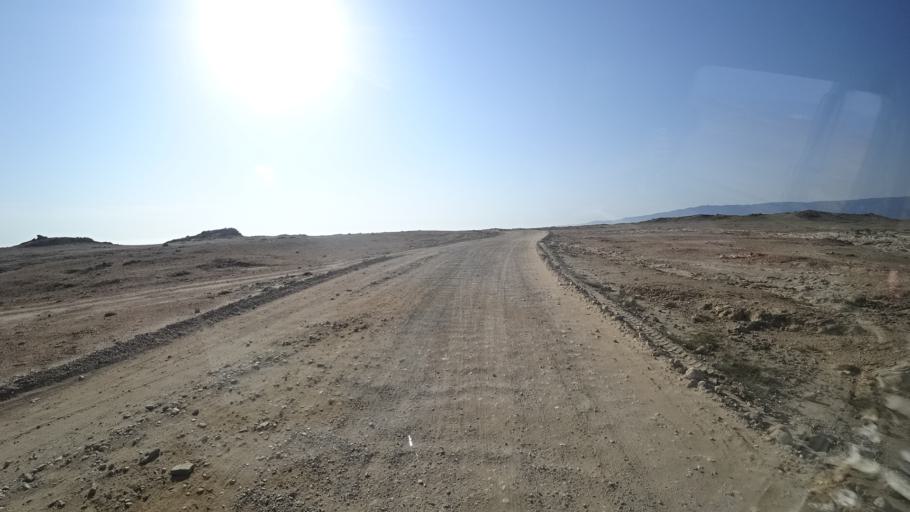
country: OM
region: Zufar
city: Salalah
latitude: 16.9468
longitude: 54.7954
